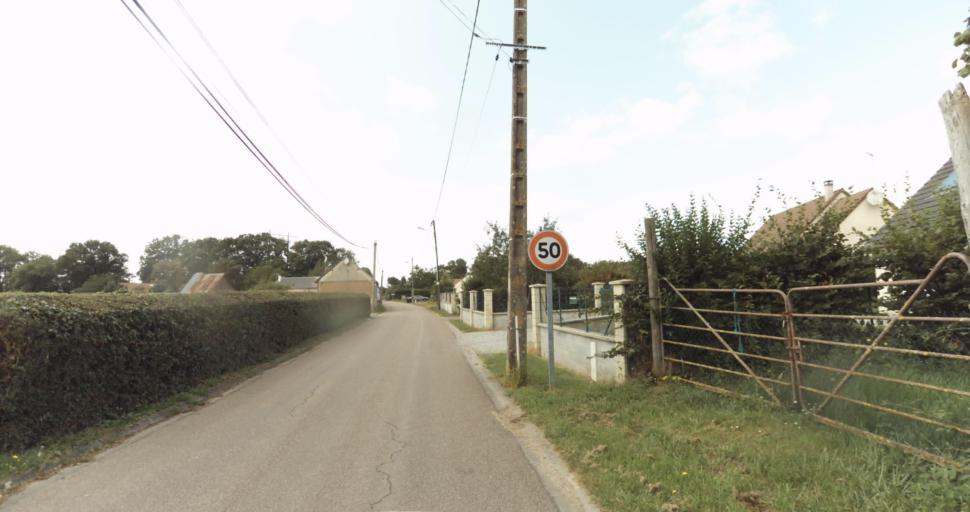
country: FR
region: Haute-Normandie
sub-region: Departement de l'Eure
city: Nonancourt
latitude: 48.8331
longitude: 1.1713
